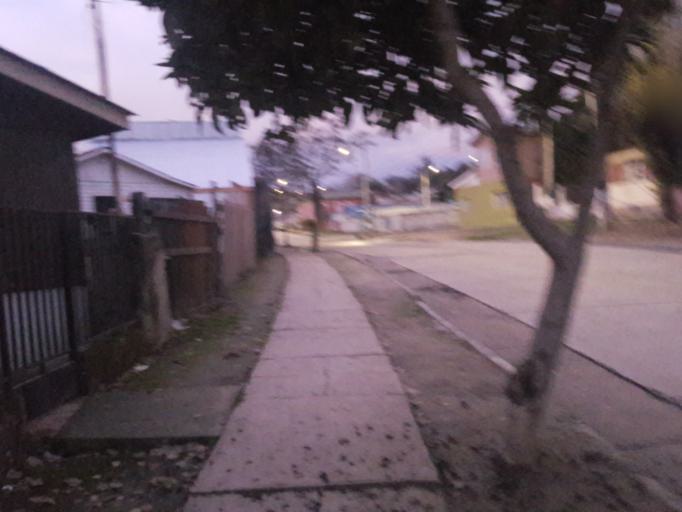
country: CL
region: Valparaiso
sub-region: Provincia de Marga Marga
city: Villa Alemana
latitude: -33.0398
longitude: -71.3511
